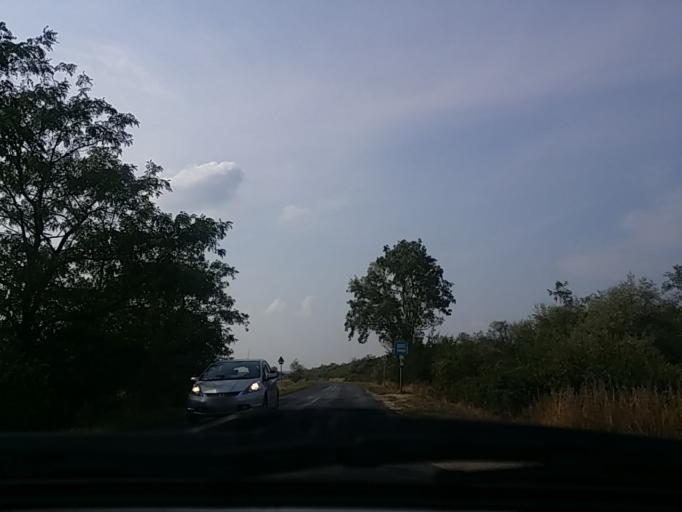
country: HU
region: Komarom-Esztergom
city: Oroszlany
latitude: 47.4843
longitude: 18.3872
